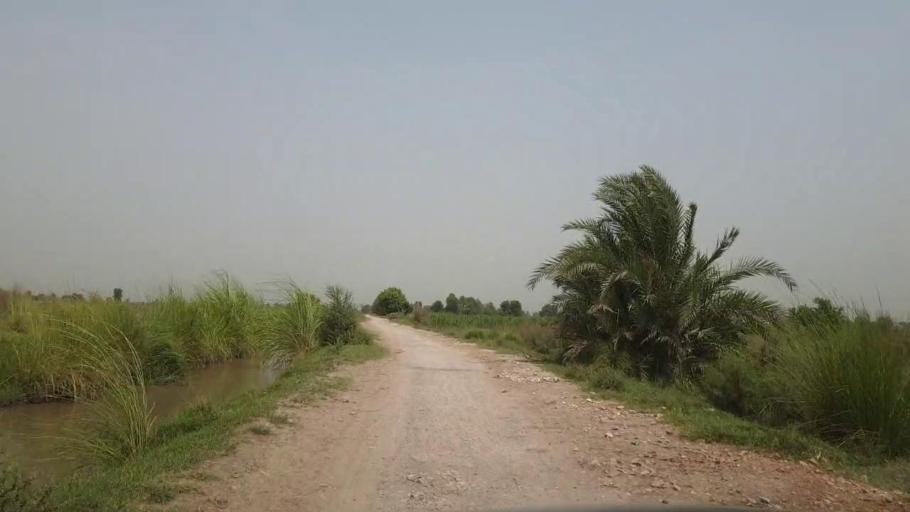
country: PK
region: Sindh
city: Gambat
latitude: 27.4507
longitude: 68.4427
